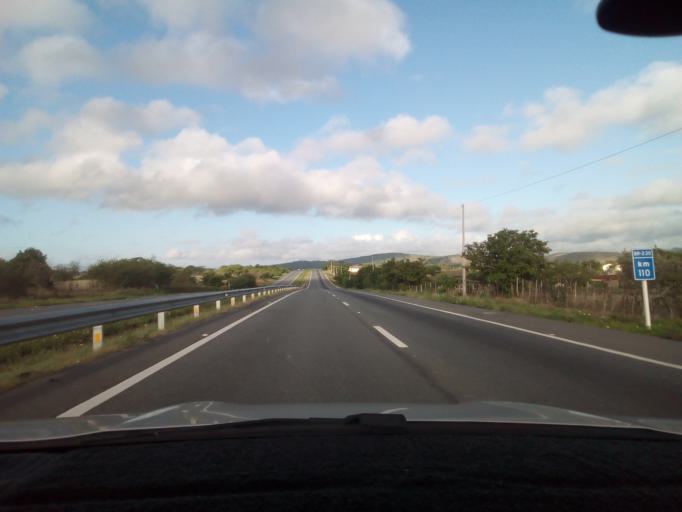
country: BR
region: Paraiba
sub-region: Serra Redonda
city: Alagoa Grande
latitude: -7.2085
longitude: -35.5732
